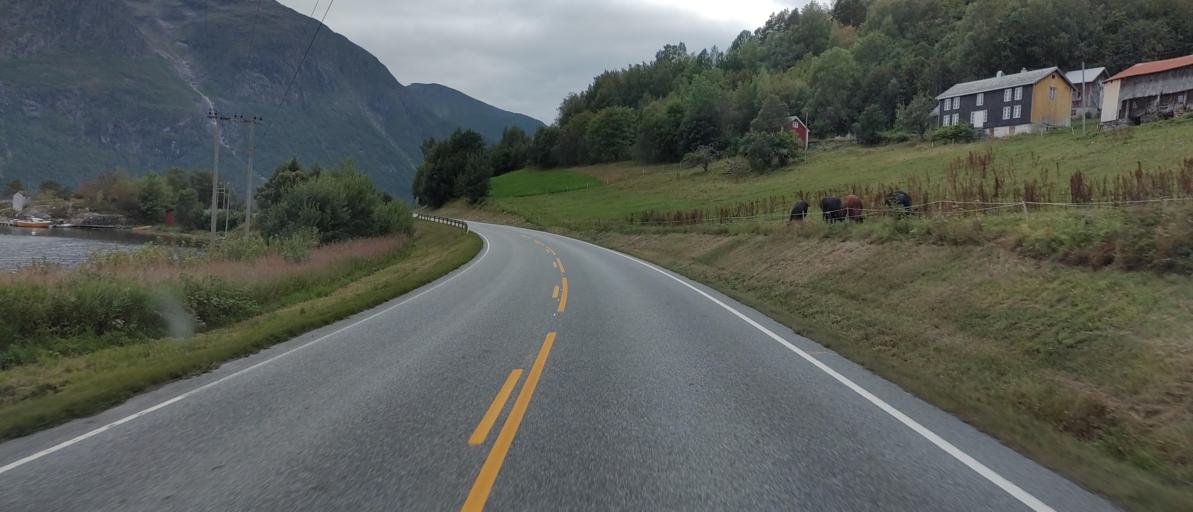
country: NO
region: More og Romsdal
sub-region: Rauma
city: Andalsnes
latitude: 62.5748
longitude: 7.6576
